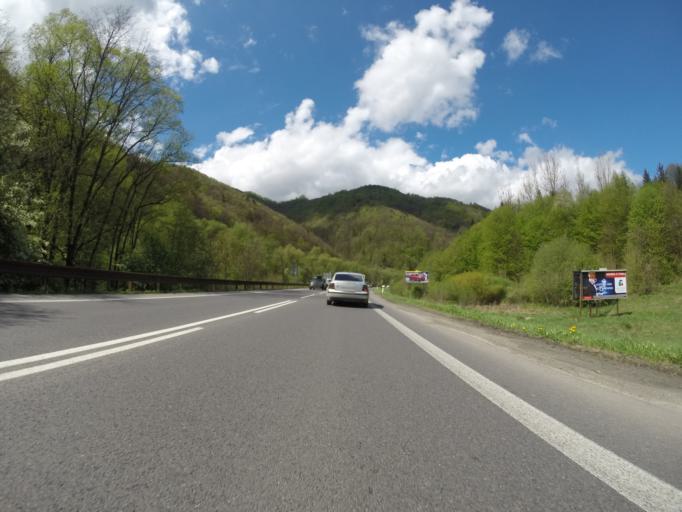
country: SK
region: Banskobystricky
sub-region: Okres Banska Bystrica
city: Brezno
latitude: 48.8029
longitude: 19.5548
